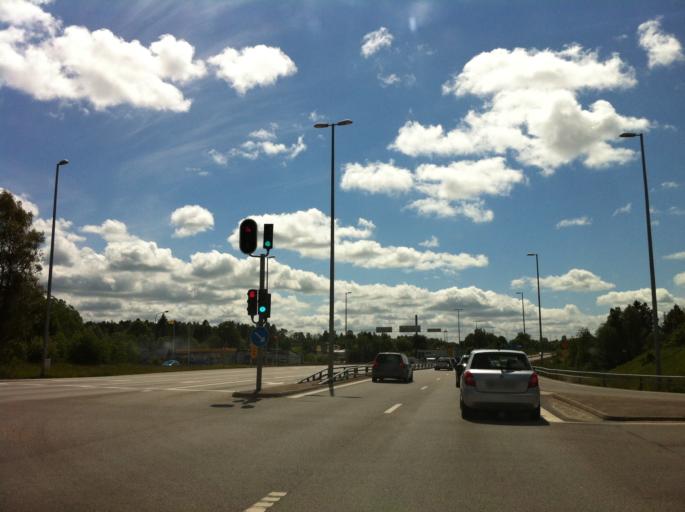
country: SE
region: Vaestra Goetaland
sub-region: Trollhattan
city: Trollhattan
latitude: 58.2631
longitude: 12.2912
